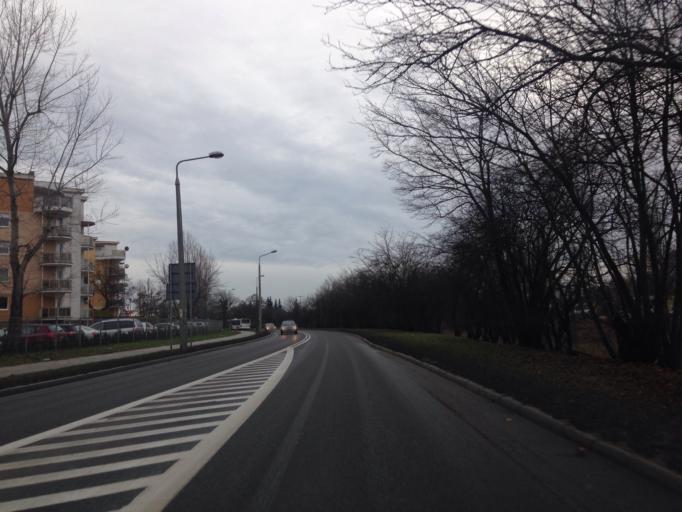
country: PL
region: Kujawsko-Pomorskie
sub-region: Torun
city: Torun
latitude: 53.0177
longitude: 18.6207
